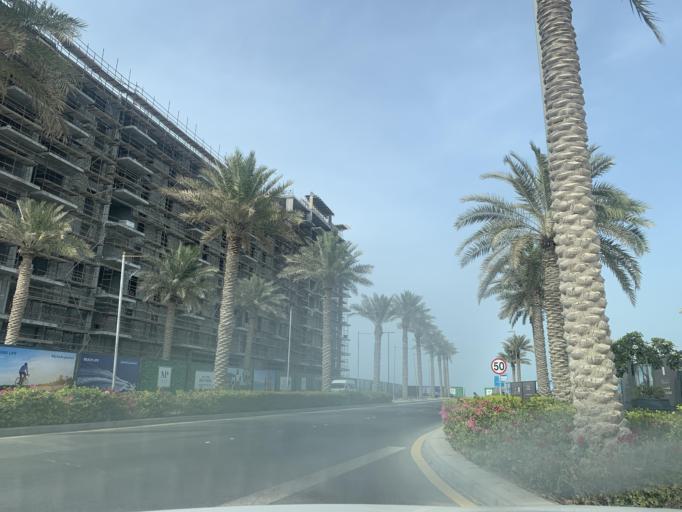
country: BH
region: Muharraq
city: Al Muharraq
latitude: 26.3069
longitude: 50.6455
